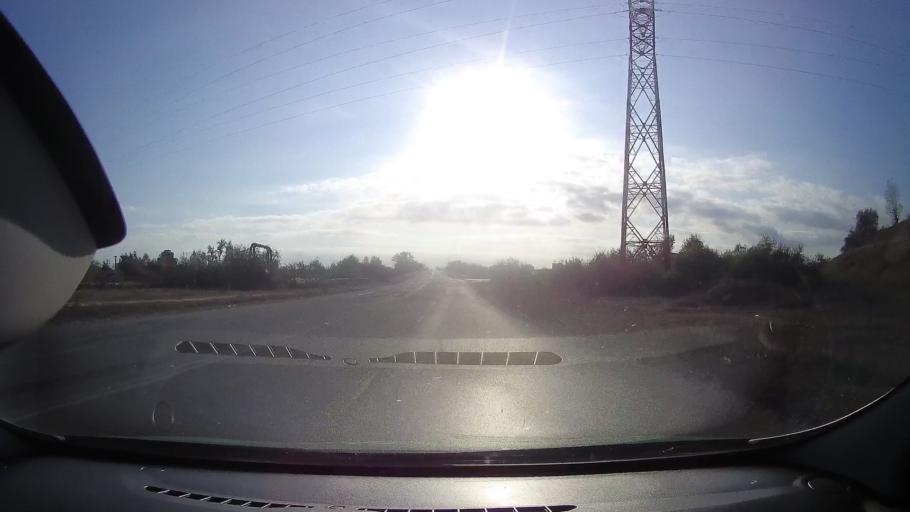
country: RO
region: Constanta
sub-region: Comuna Navodari
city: Navodari
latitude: 44.3266
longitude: 28.6257
